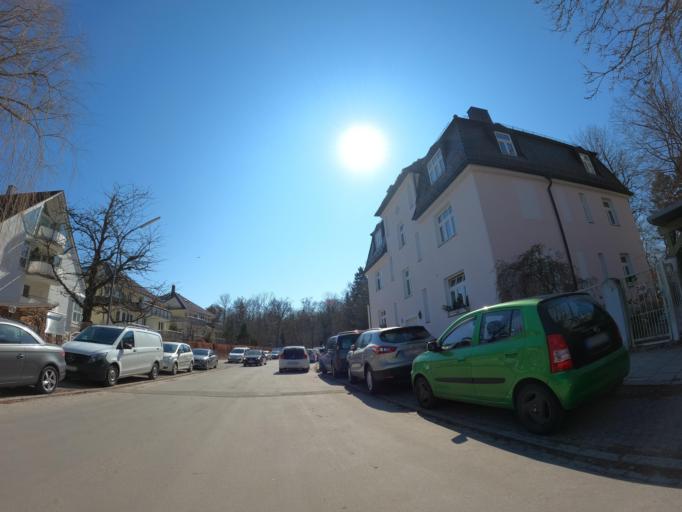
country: DE
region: Bavaria
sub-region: Upper Bavaria
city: Pullach im Isartal
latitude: 48.0860
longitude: 11.5612
